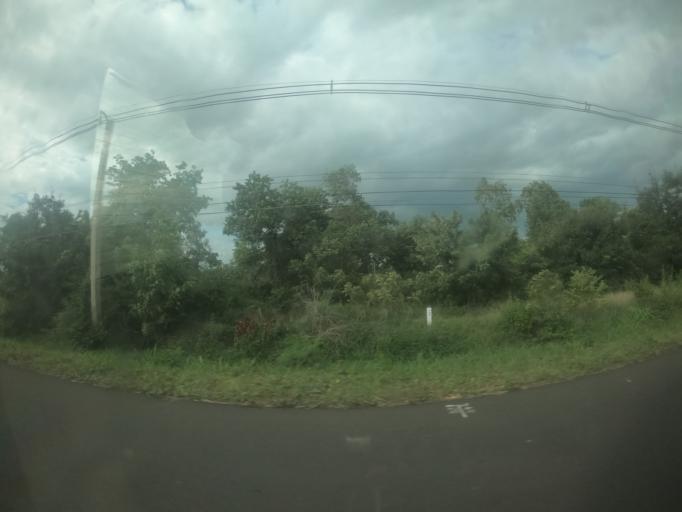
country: TH
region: Surin
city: Kap Choeng
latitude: 14.5329
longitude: 103.5286
